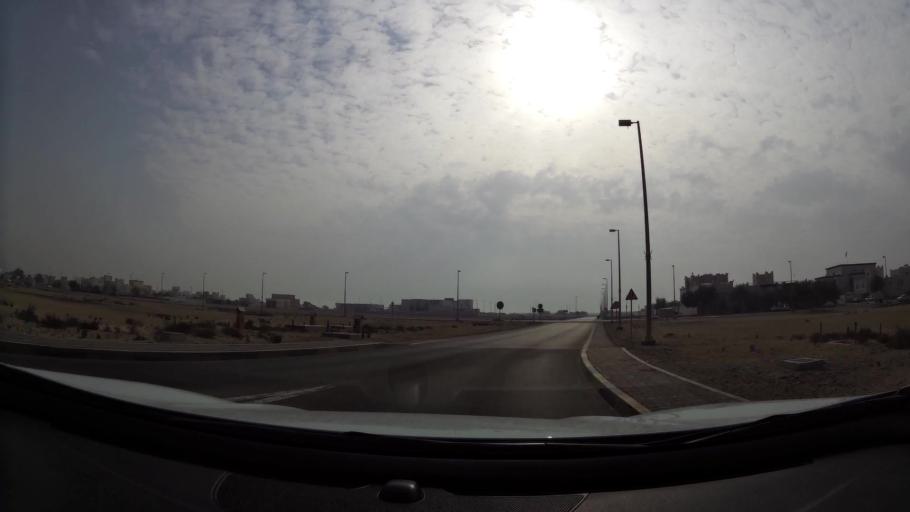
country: AE
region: Abu Dhabi
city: Abu Dhabi
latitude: 24.6661
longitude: 54.7697
